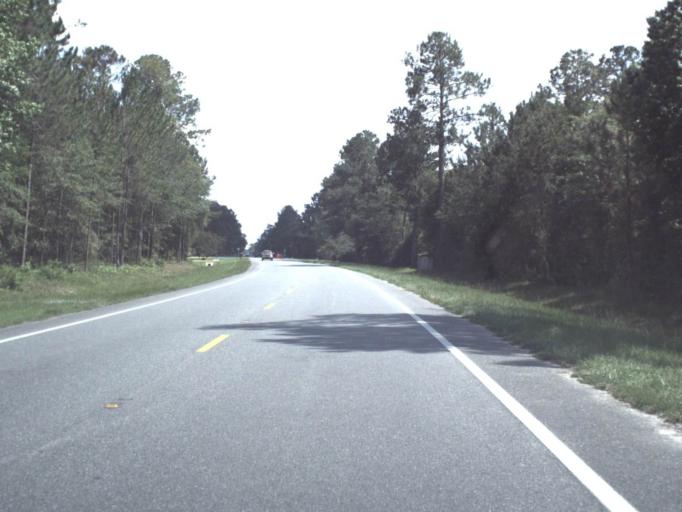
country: US
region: Florida
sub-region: Baker County
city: Macclenny
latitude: 30.2949
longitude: -82.1264
